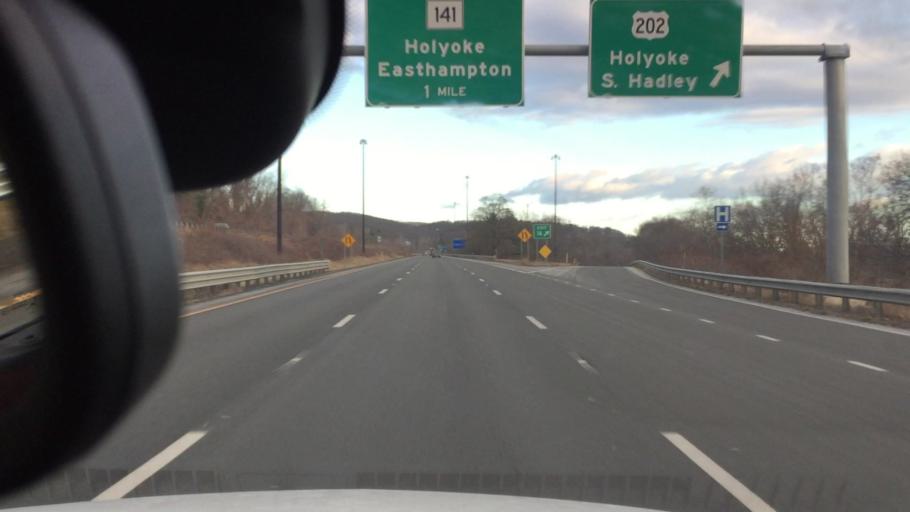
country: US
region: Massachusetts
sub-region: Hampden County
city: Holyoke
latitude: 42.1958
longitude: -72.6378
